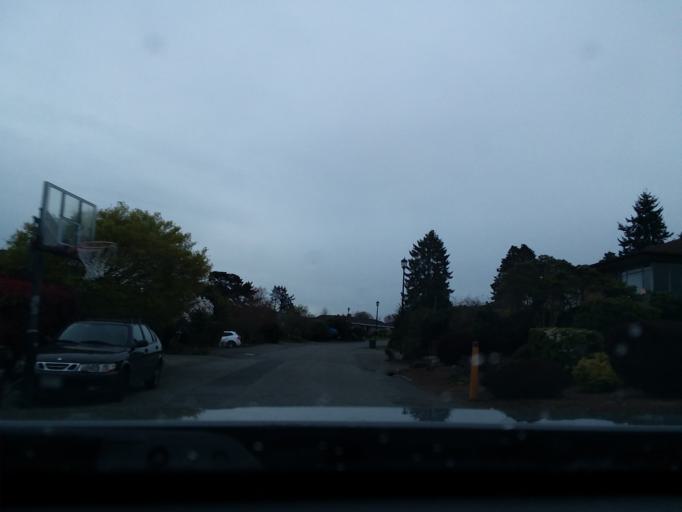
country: US
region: Washington
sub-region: King County
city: Shoreline
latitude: 47.7072
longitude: -122.3726
